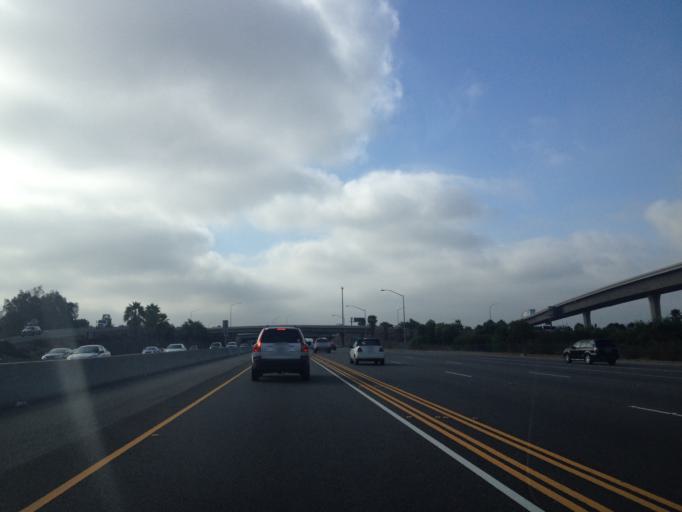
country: US
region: California
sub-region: Orange County
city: Laguna Woods
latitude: 33.6477
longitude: -117.7377
